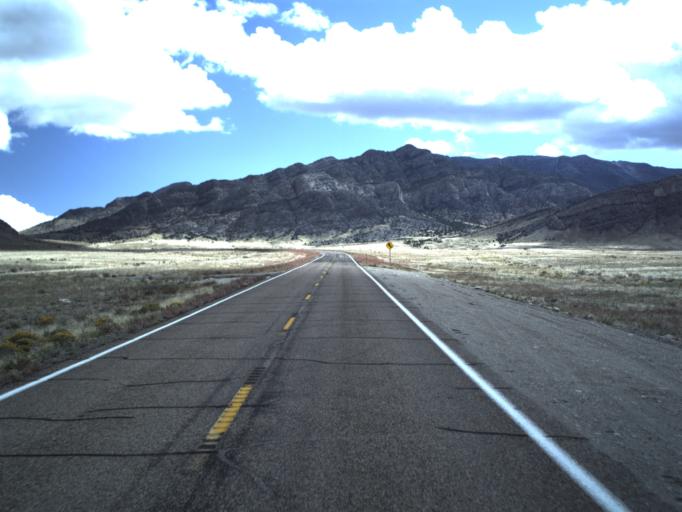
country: US
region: Utah
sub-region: Beaver County
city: Milford
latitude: 38.5083
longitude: -113.6172
